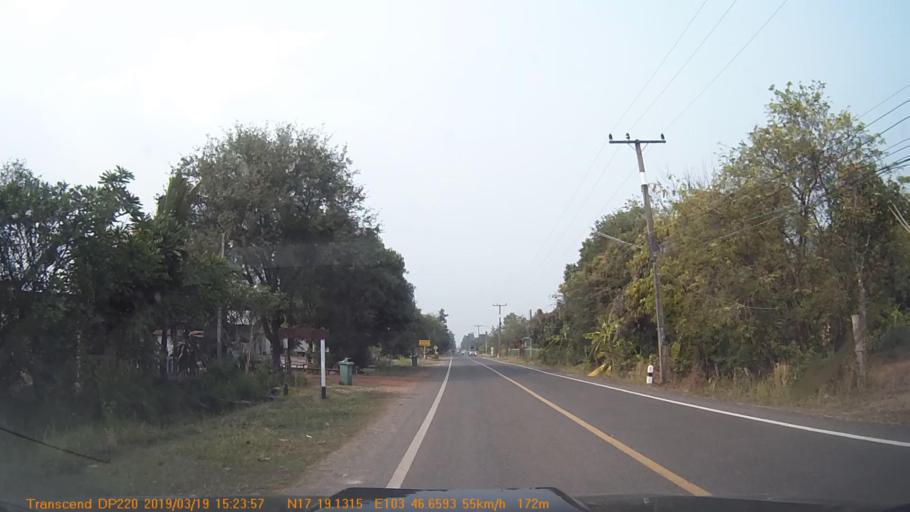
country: TH
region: Sakon Nakhon
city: Phanna Nikhom
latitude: 17.3190
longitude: 103.7777
